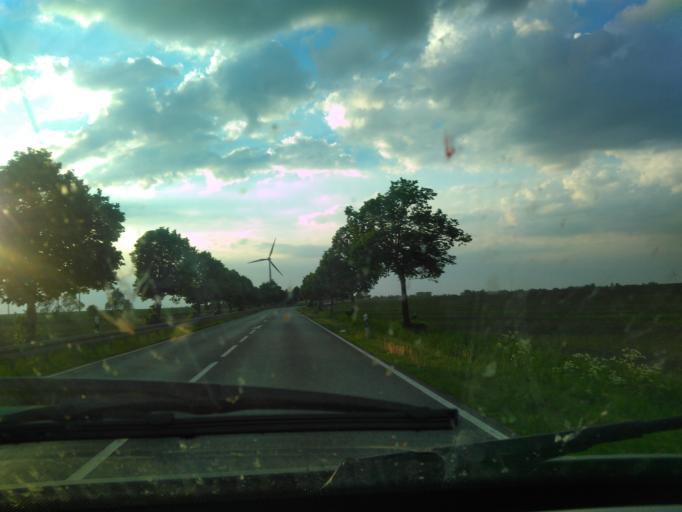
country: DE
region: Saxony-Anhalt
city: Osterfeld
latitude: 51.0987
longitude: 11.9405
